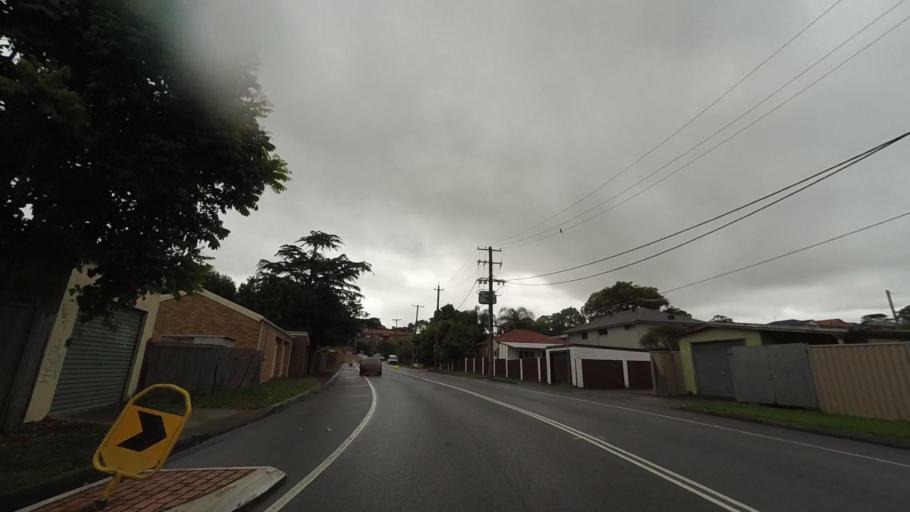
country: AU
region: New South Wales
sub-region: Kogarah
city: Kogarah Bay
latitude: -33.9744
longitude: 151.1187
